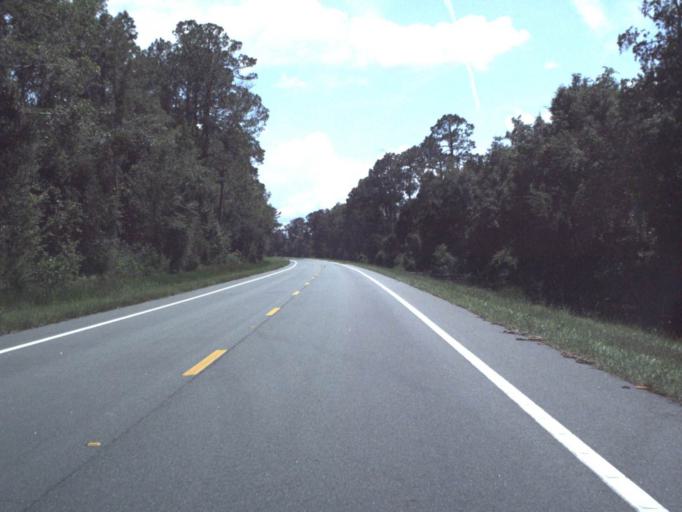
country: US
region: Florida
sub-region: Hamilton County
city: Jasper
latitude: 30.5406
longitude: -82.6788
